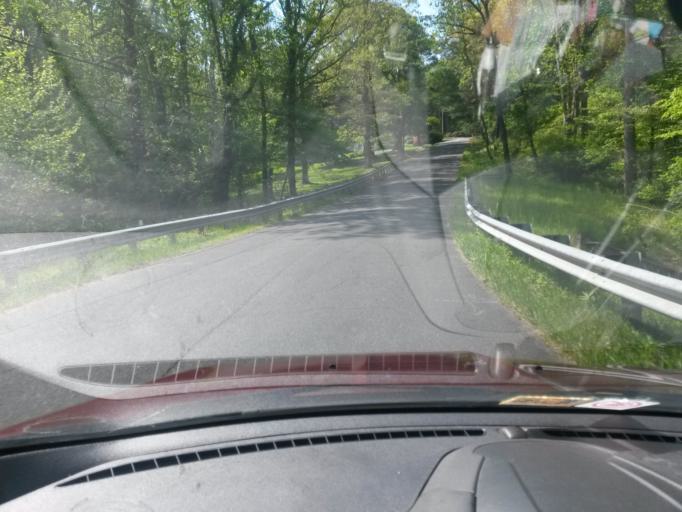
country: US
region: Virginia
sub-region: Campbell County
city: Timberlake
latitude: 37.3509
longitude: -79.2190
